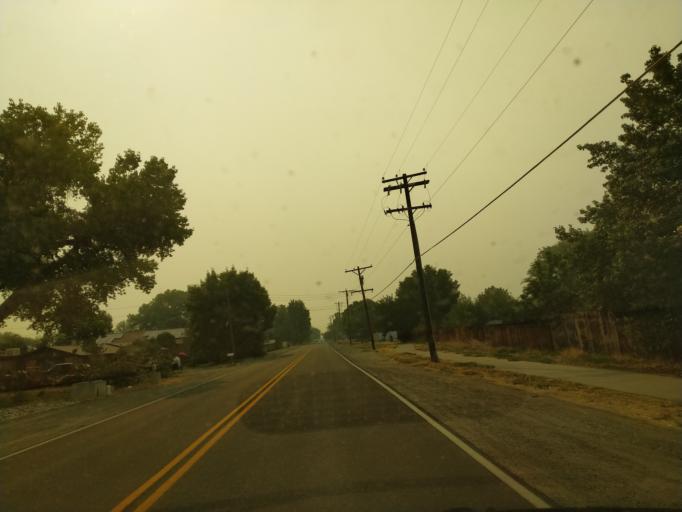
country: US
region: Colorado
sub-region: Mesa County
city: Fruitvale
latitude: 39.0846
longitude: -108.4796
